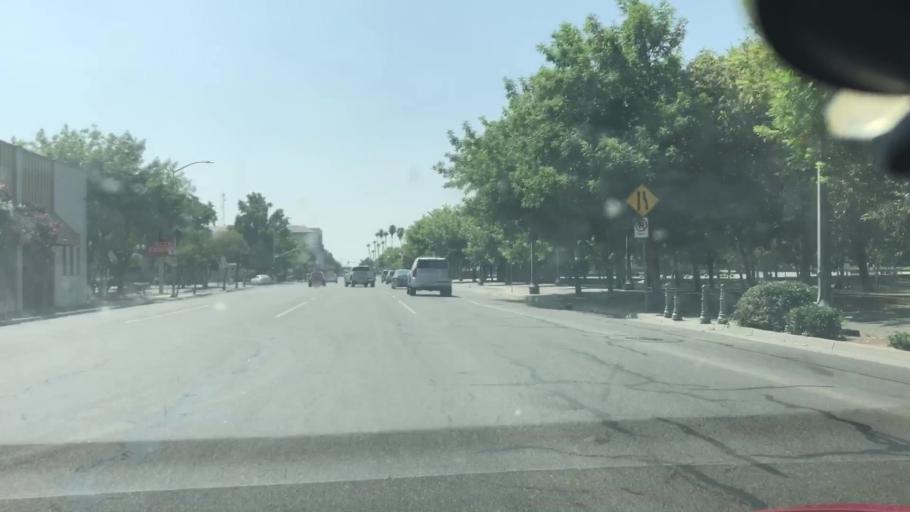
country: US
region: California
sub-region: San Joaquin County
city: Stockton
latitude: 37.9566
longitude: -121.2922
